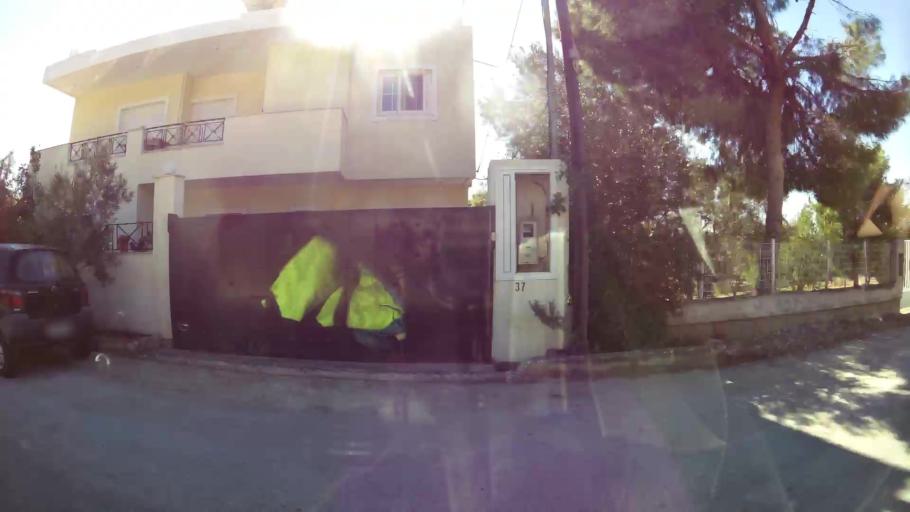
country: GR
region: Attica
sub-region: Nomarchia Anatolikis Attikis
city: Kitsi
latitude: 37.8485
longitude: 23.8222
